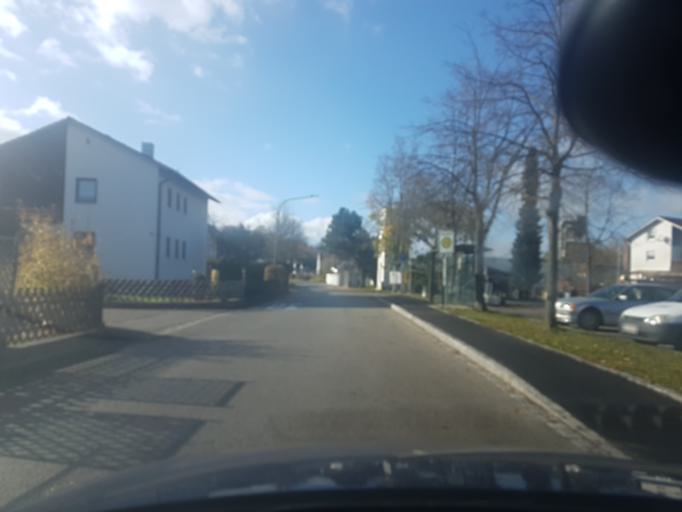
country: DE
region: Bavaria
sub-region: Lower Bavaria
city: Loiching
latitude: 48.6260
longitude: 12.4596
